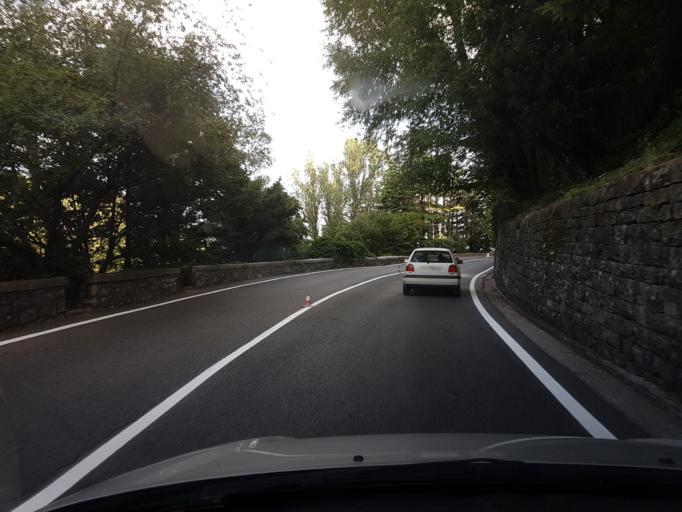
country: IT
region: Friuli Venezia Giulia
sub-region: Provincia di Trieste
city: Prosecco-Contovello
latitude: 45.7019
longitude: 13.7342
